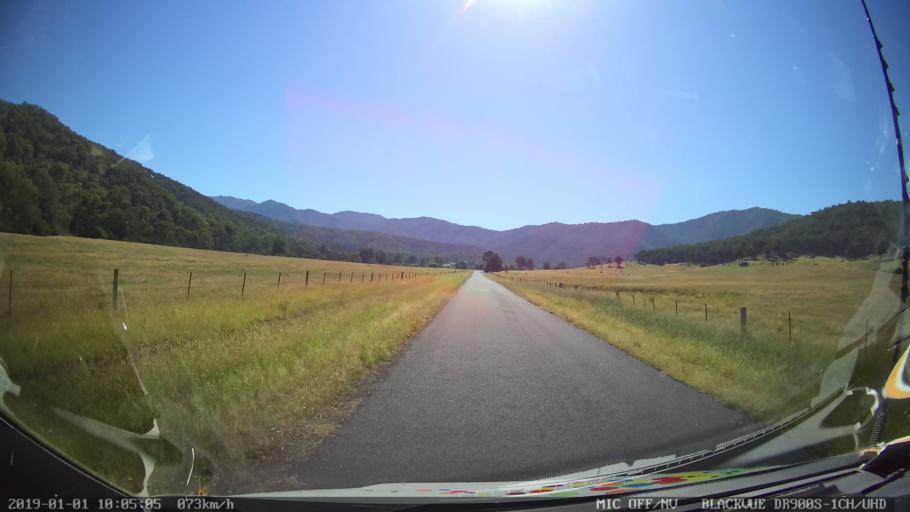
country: AU
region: New South Wales
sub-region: Snowy River
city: Jindabyne
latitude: -36.1743
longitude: 148.1312
